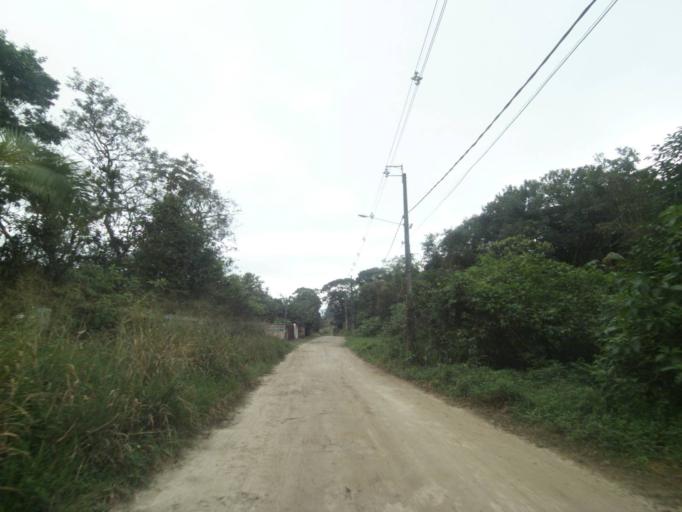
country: BR
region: Parana
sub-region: Paranagua
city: Paranagua
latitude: -25.5414
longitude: -48.5547
